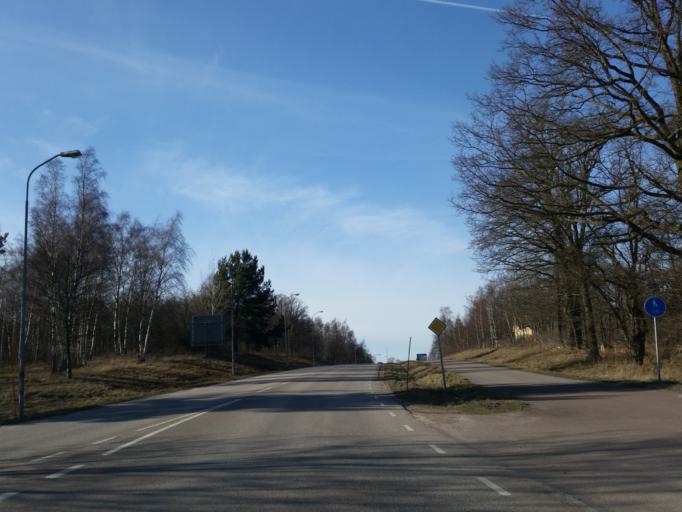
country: SE
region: Kalmar
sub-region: Kalmar Kommun
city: Kalmar
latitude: 56.6783
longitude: 16.3175
